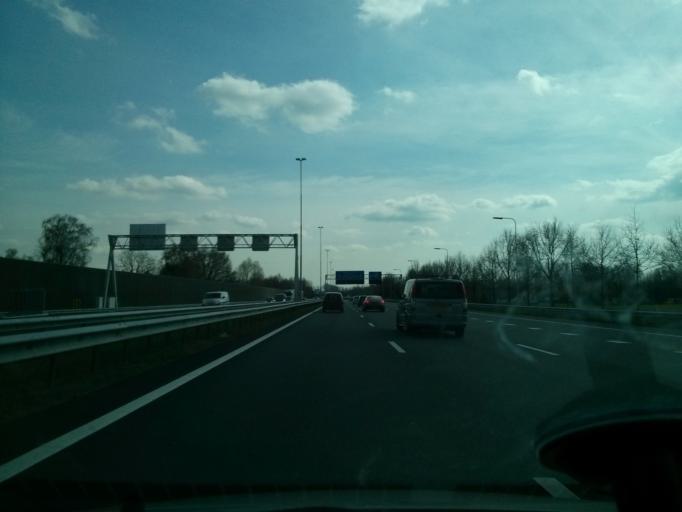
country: NL
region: North Brabant
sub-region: Gemeente Boxtel
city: Boxtel
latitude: 51.5718
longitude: 5.3563
